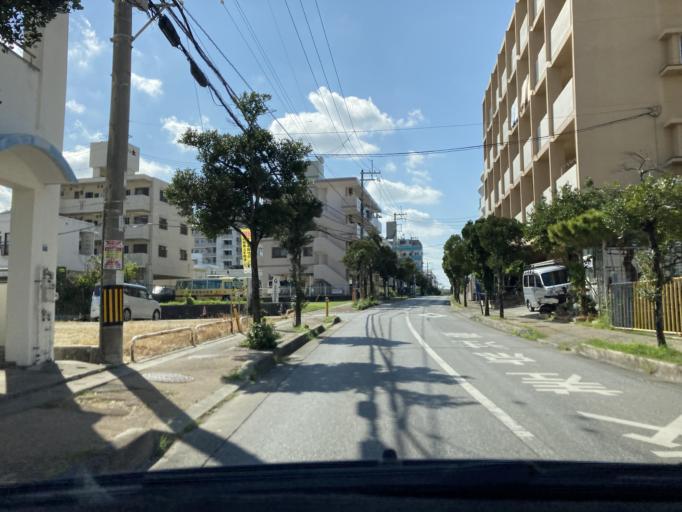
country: JP
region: Okinawa
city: Tomigusuku
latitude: 26.1857
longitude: 127.6569
